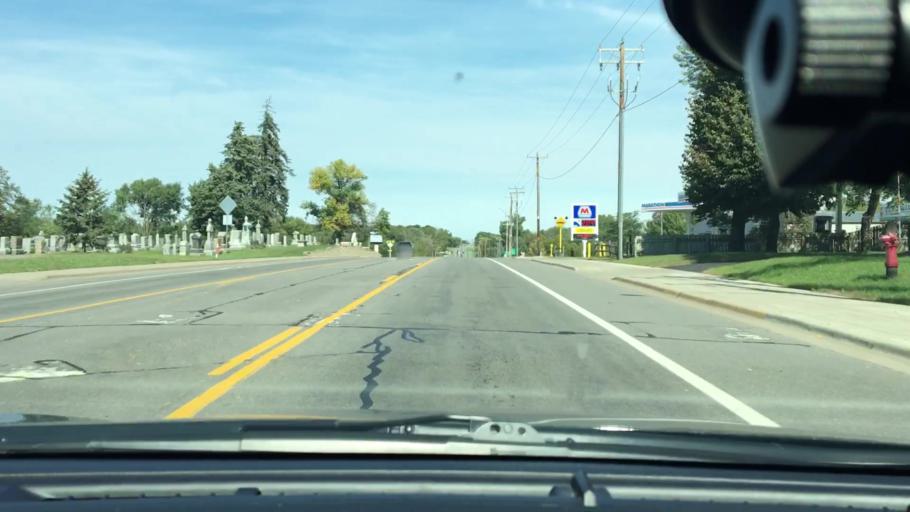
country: US
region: Minnesota
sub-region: Wright County
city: Hanover
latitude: 45.1568
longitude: -93.6660
